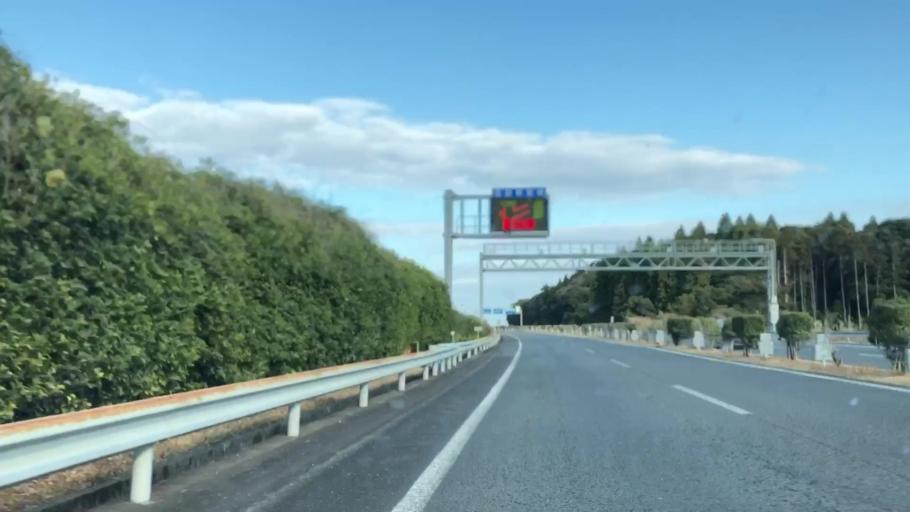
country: JP
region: Miyazaki
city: Miyazaki-shi
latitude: 31.8684
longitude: 131.4101
